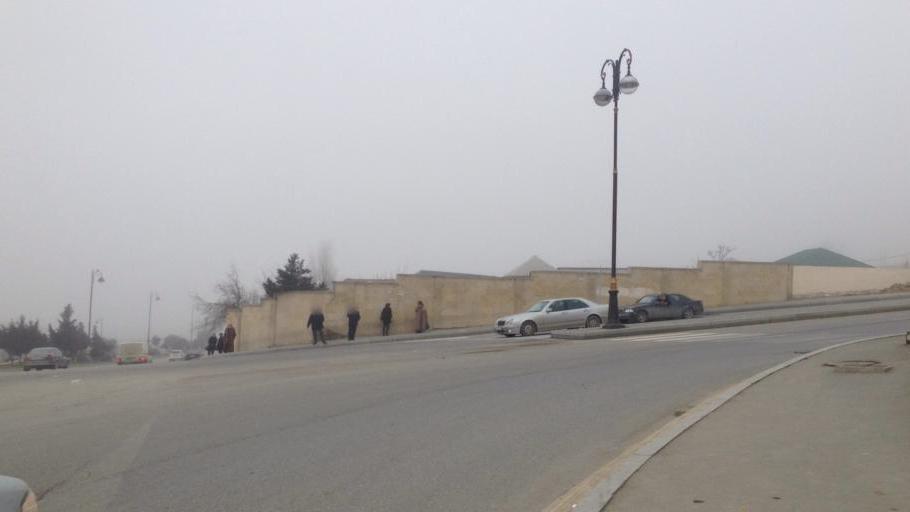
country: AZ
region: Baki
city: Qaracuxur
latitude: 40.3497
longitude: 49.9606
